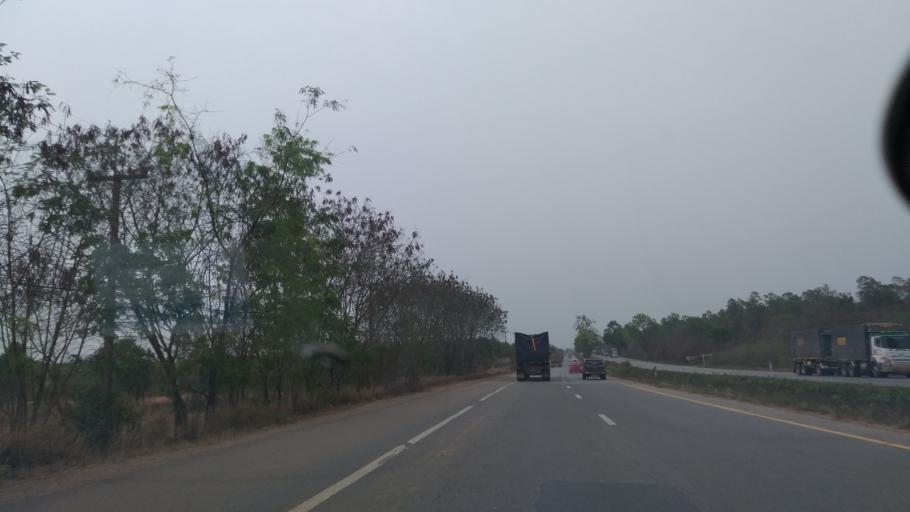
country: TH
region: Chachoengsao
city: Plaeng Yao
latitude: 13.5321
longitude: 101.2629
